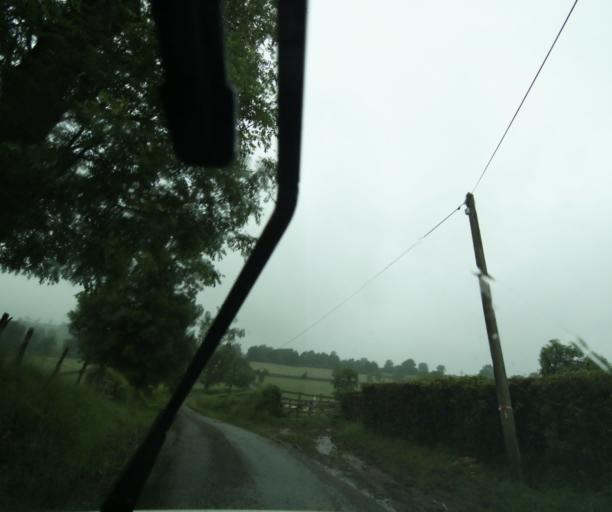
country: FR
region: Bourgogne
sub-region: Departement de Saone-et-Loire
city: Charolles
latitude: 46.4018
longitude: 4.2449
